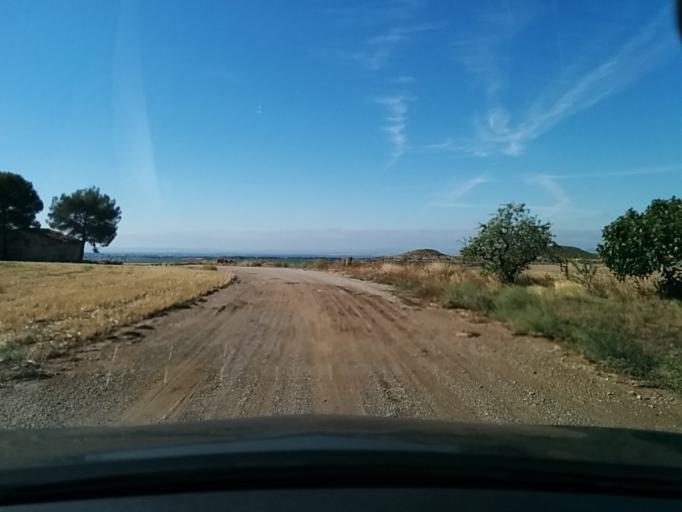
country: ES
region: Aragon
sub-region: Provincia de Zaragoza
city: Tauste
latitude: 42.0132
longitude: -1.3038
